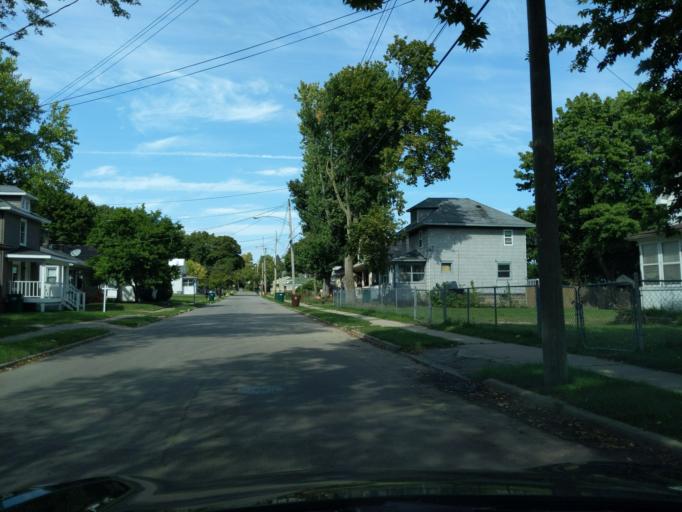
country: US
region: Michigan
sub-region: Ingham County
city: Lansing
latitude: 42.7147
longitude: -84.5419
